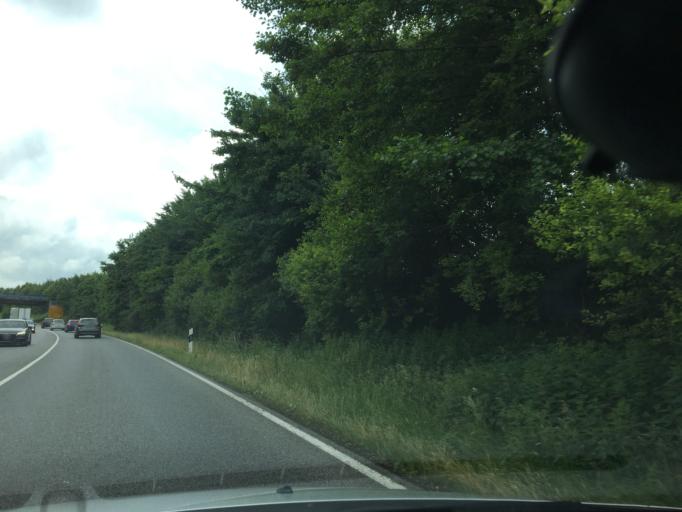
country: DE
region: Bavaria
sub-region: Upper Bavaria
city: Moosinning
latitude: 48.2633
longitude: 11.8584
